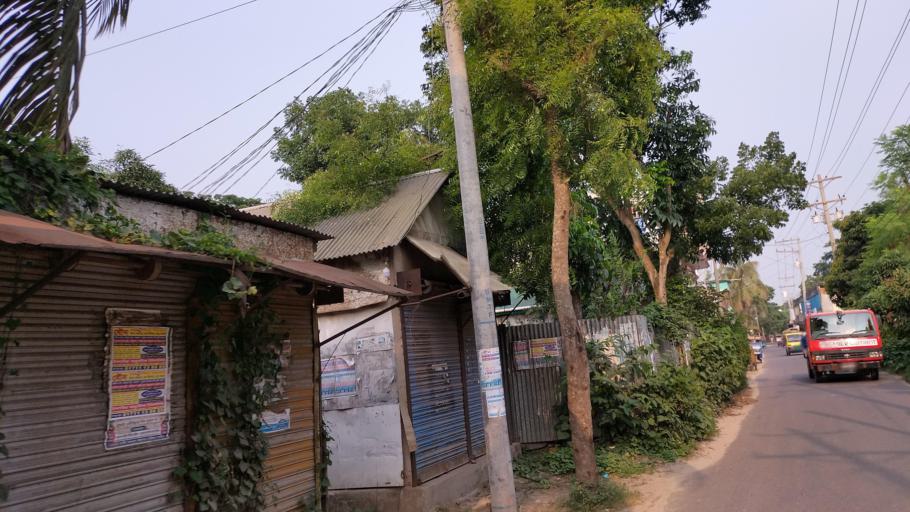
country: BD
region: Dhaka
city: Azimpur
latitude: 23.6675
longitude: 90.3250
